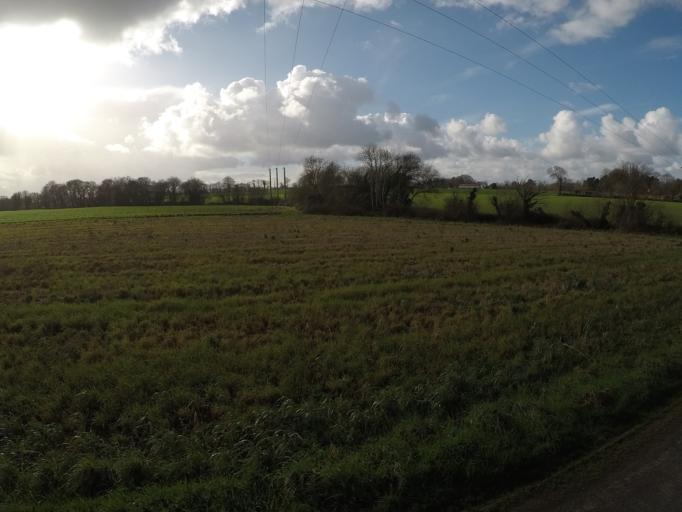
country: FR
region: Brittany
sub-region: Departement des Cotes-d'Armor
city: Goudelin
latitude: 48.6136
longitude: -2.9996
